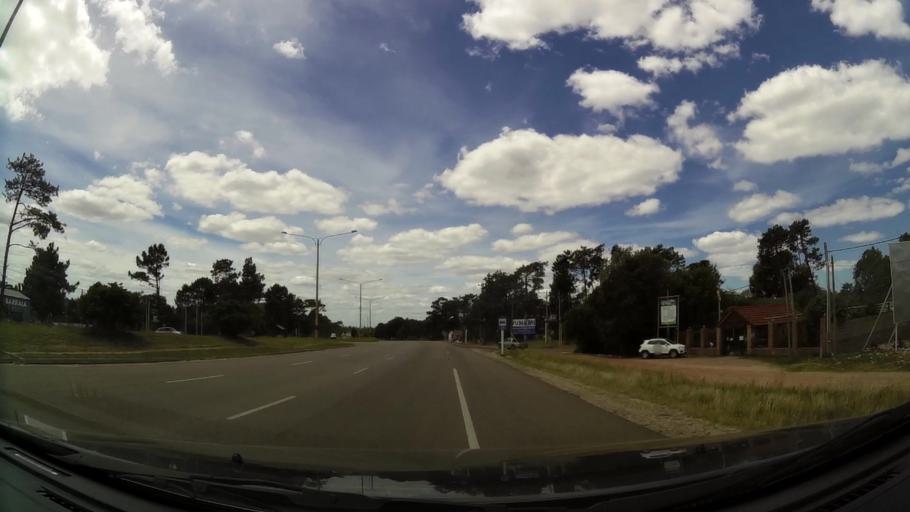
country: UY
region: Canelones
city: Pando
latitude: -34.7939
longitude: -55.9021
